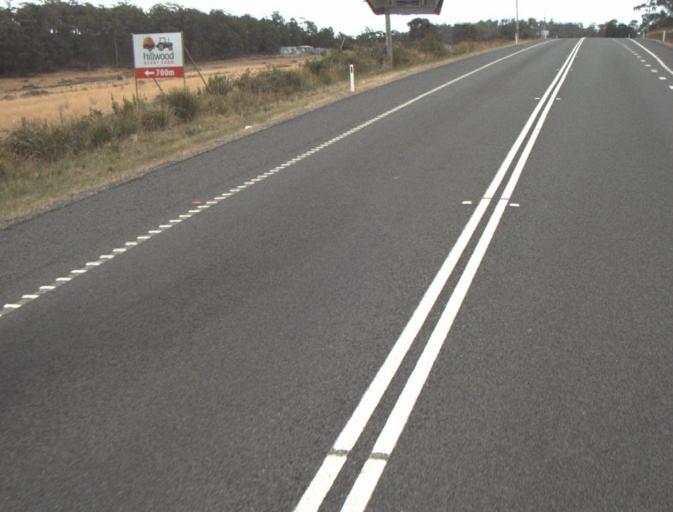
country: AU
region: Tasmania
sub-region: Launceston
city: Mayfield
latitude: -41.2515
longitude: 147.0222
